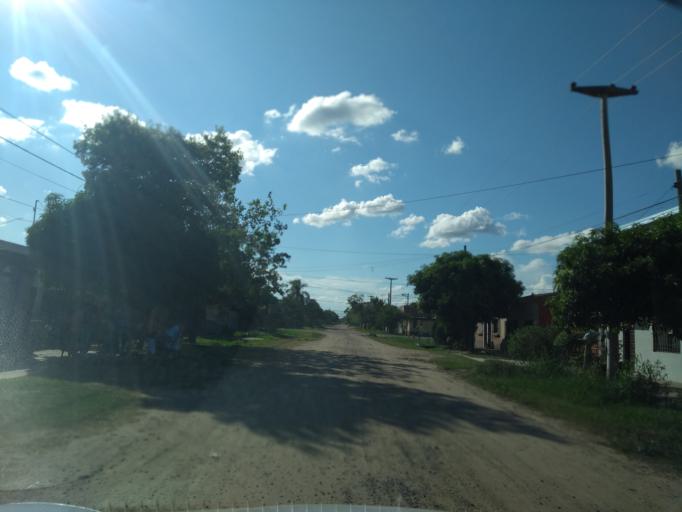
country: AR
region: Chaco
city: Resistencia
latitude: -27.4780
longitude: -58.9778
